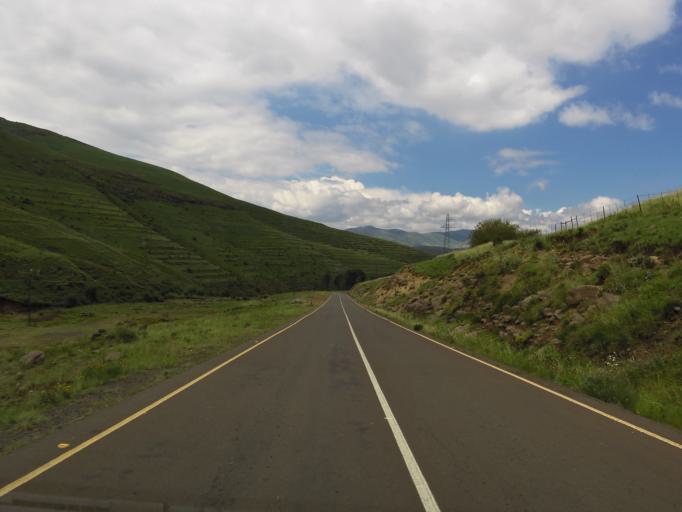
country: LS
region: Butha-Buthe
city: Butha-Buthe
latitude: -29.1102
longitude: 28.4636
